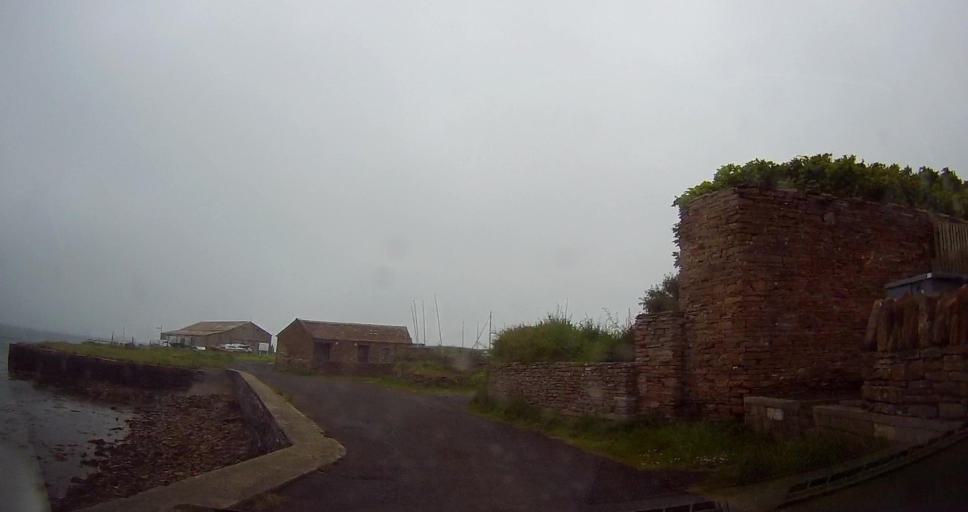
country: GB
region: Scotland
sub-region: Orkney Islands
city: Stromness
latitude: 58.9537
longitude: -3.2990
